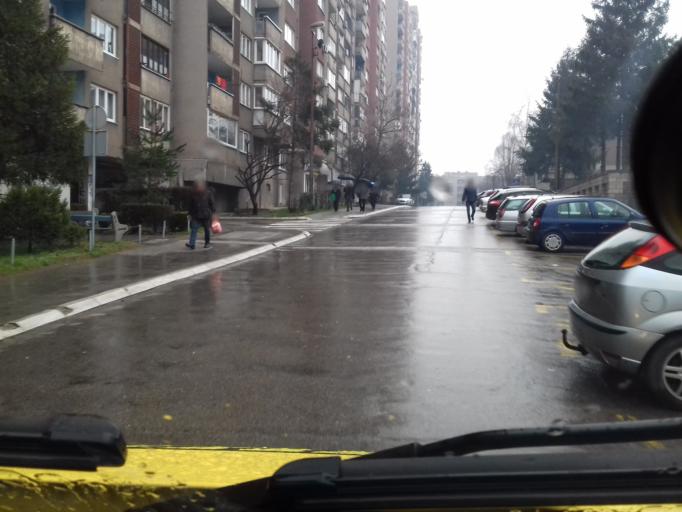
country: BA
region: Federation of Bosnia and Herzegovina
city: Zenica
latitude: 44.1984
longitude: 17.9094
